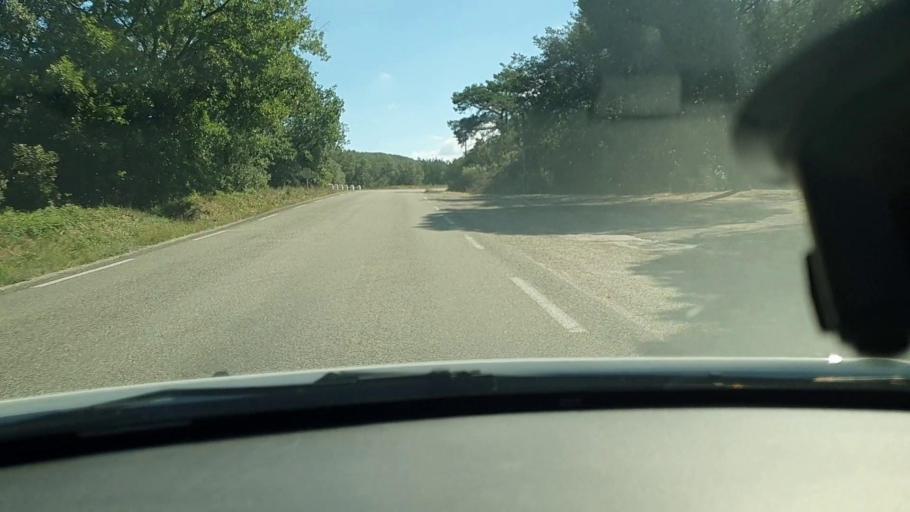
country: FR
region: Languedoc-Roussillon
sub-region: Departement du Gard
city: Goudargues
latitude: 44.1739
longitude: 4.4871
